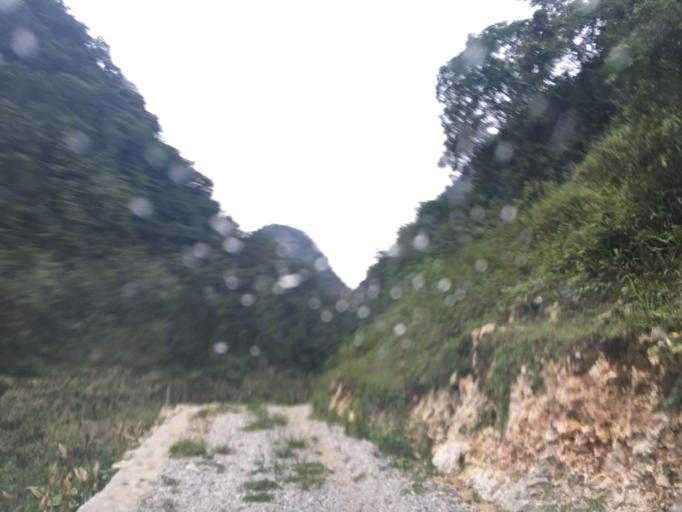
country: CN
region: Guangxi Zhuangzu Zizhiqu
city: Xinzhou
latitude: 25.2257
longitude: 105.6278
